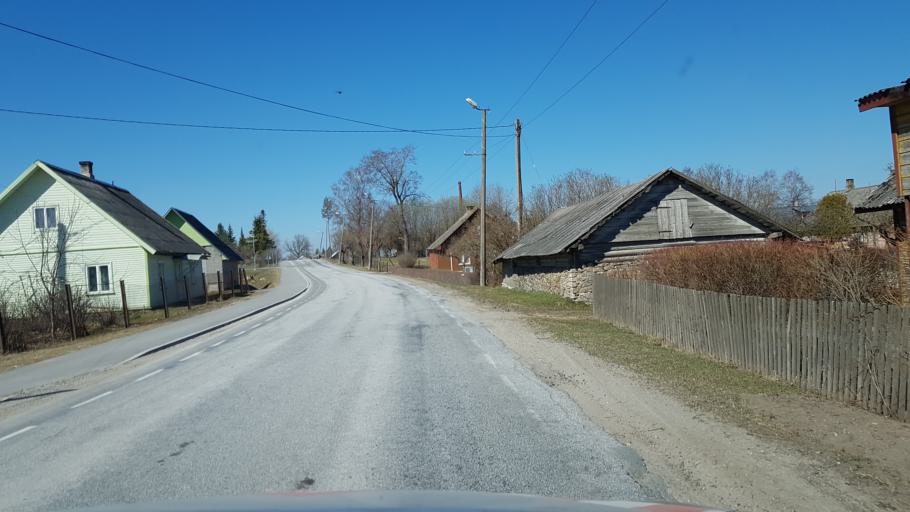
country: EE
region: Laeaene-Virumaa
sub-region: Rakke vald
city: Rakke
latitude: 58.9851
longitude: 26.2518
